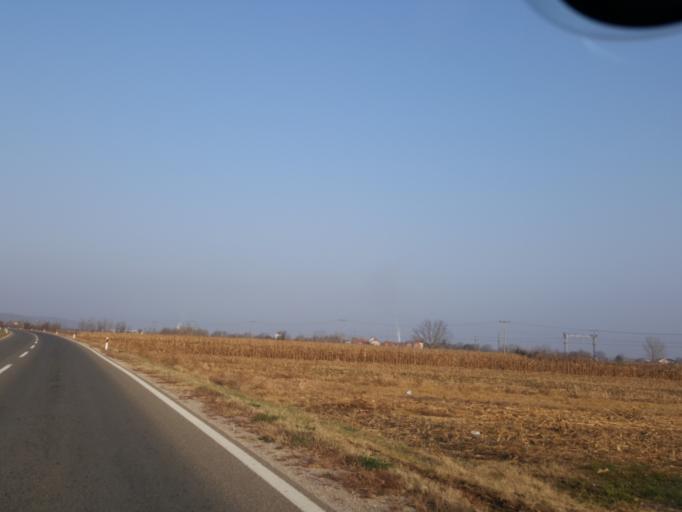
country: RS
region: Central Serbia
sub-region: Jablanicki Okrug
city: Leskovac
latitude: 42.9334
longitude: 22.0119
